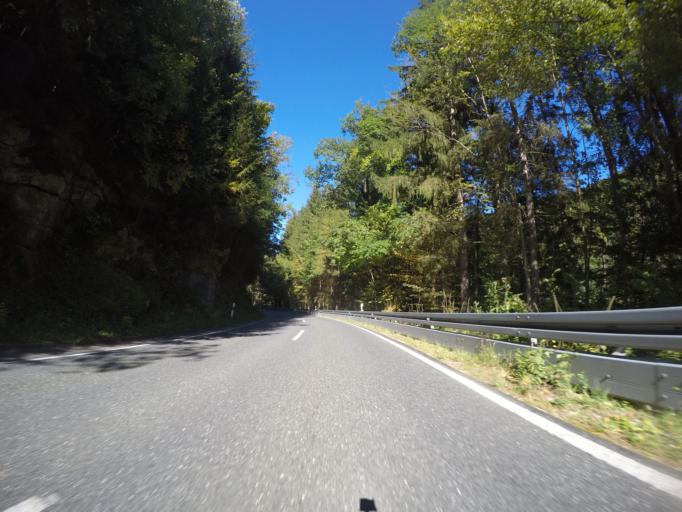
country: DE
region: Bavaria
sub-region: Upper Franconia
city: Gossweinstein
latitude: 49.7943
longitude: 11.3316
